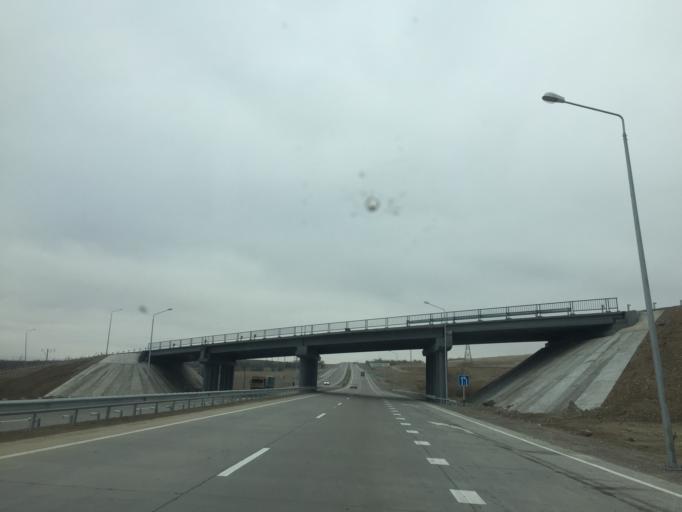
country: KZ
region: Ongtustik Qazaqstan
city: Sastobe
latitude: 42.5302
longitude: 70.0200
